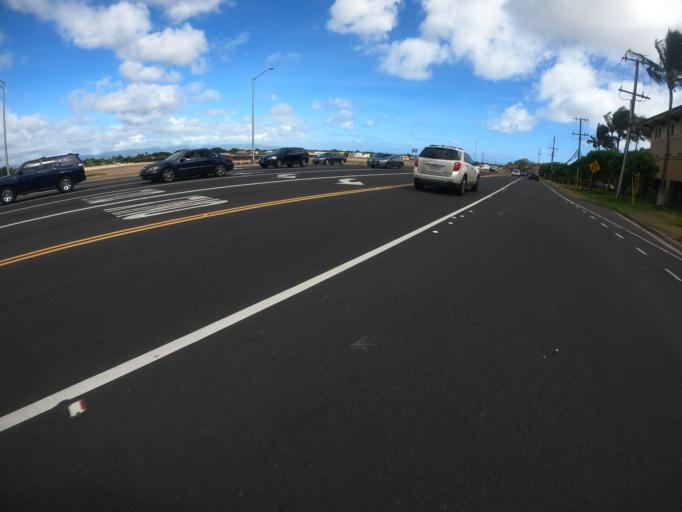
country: US
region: Hawaii
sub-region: Honolulu County
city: Makakilo City
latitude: 21.3398
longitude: -158.0759
